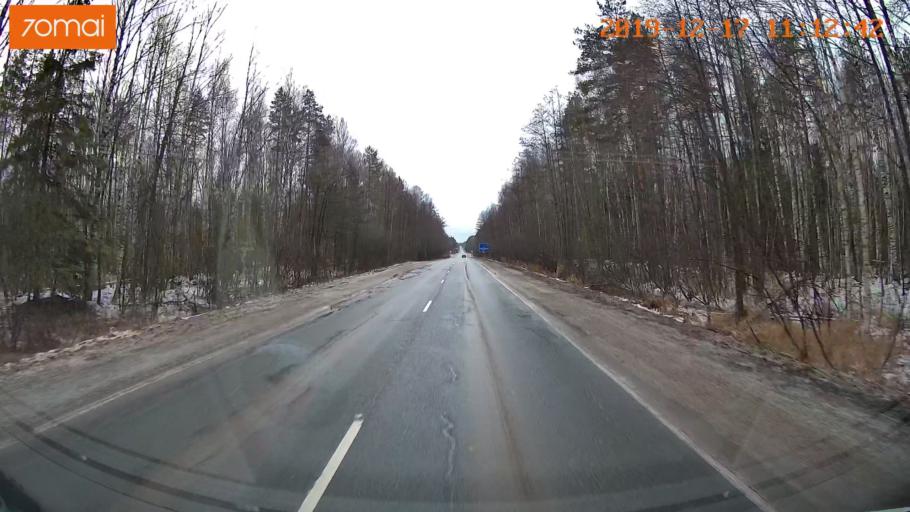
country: RU
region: Vladimir
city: Gus'-Khrustal'nyy
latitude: 55.5725
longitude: 40.6259
